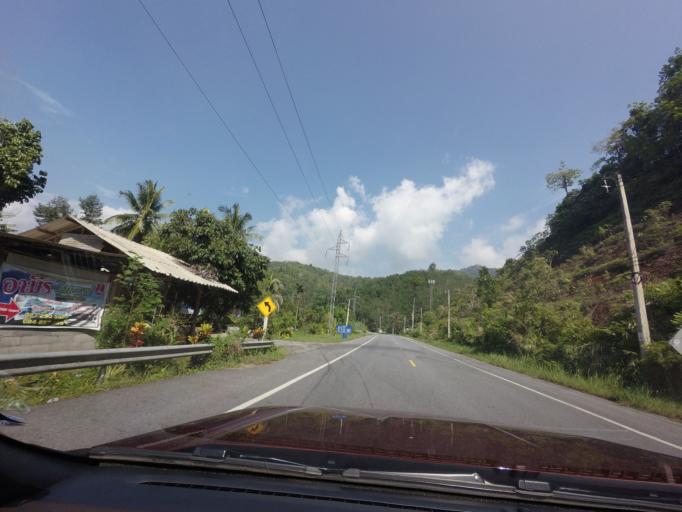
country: TH
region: Yala
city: Than To
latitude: 5.9657
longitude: 101.1980
